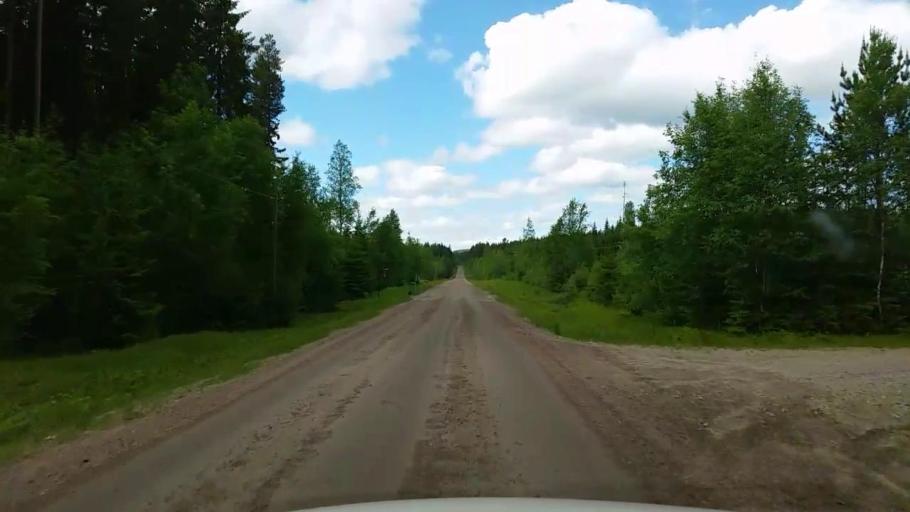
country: SE
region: Gaevleborg
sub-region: Ovanakers Kommun
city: Alfta
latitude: 61.4859
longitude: 15.9893
